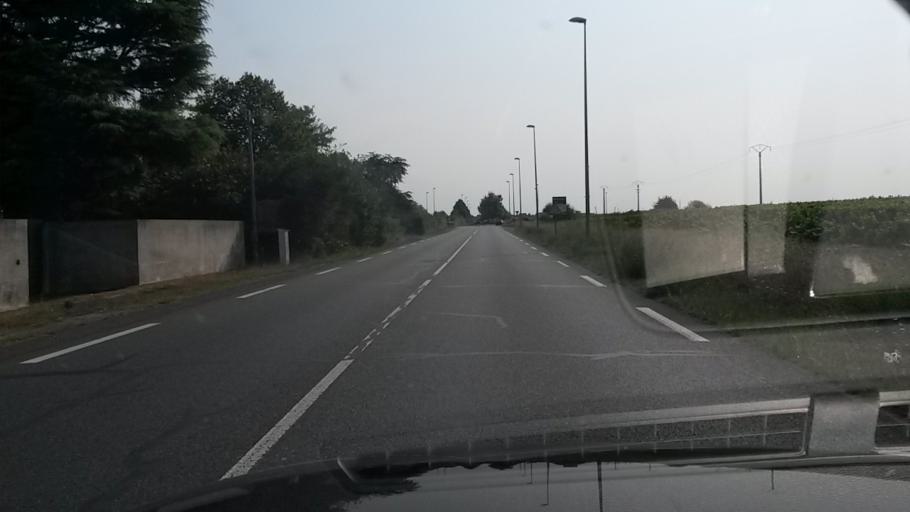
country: FR
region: Pays de la Loire
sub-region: Departement de la Loire-Atlantique
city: Mouzillon
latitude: 47.1466
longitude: -1.2809
